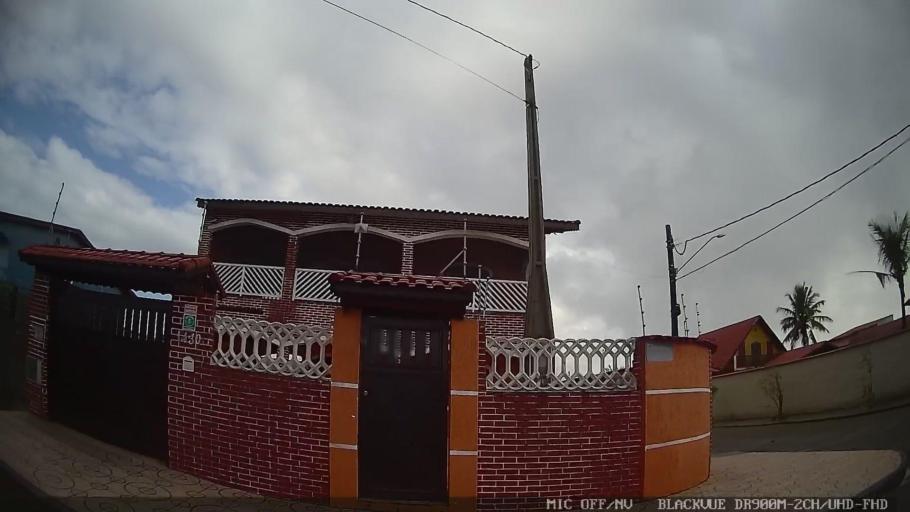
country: BR
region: Sao Paulo
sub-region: Itanhaem
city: Itanhaem
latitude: -24.2072
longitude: -46.8392
